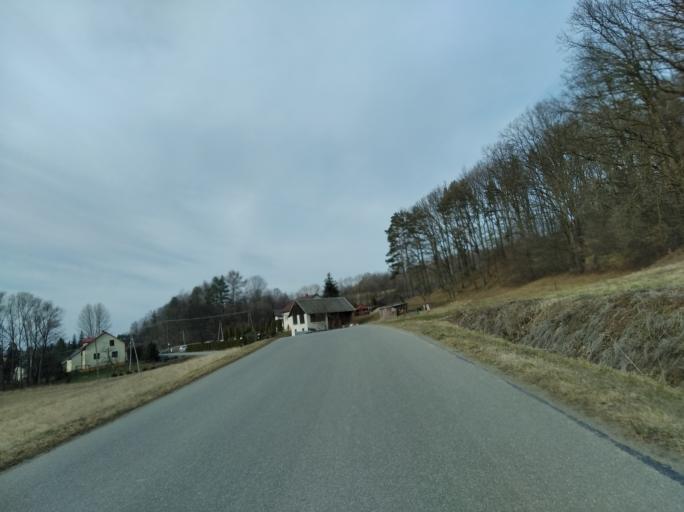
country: PL
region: Subcarpathian Voivodeship
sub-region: Powiat brzozowski
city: Gorki
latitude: 49.6390
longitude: 22.0562
